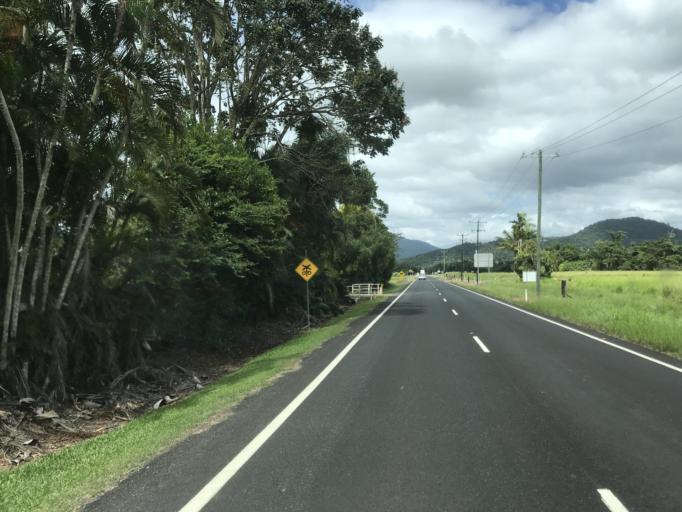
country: AU
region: Queensland
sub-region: Cassowary Coast
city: Innisfail
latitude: -17.8104
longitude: 146.0194
